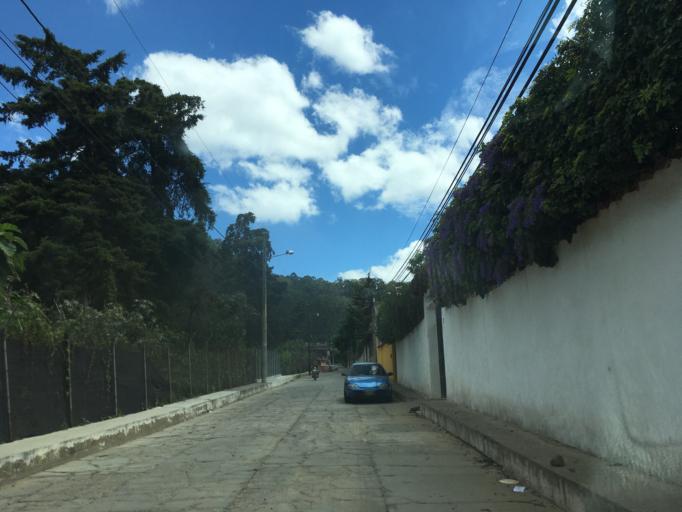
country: GT
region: Sacatepequez
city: Antigua Guatemala
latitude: 14.5639
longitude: -90.7266
